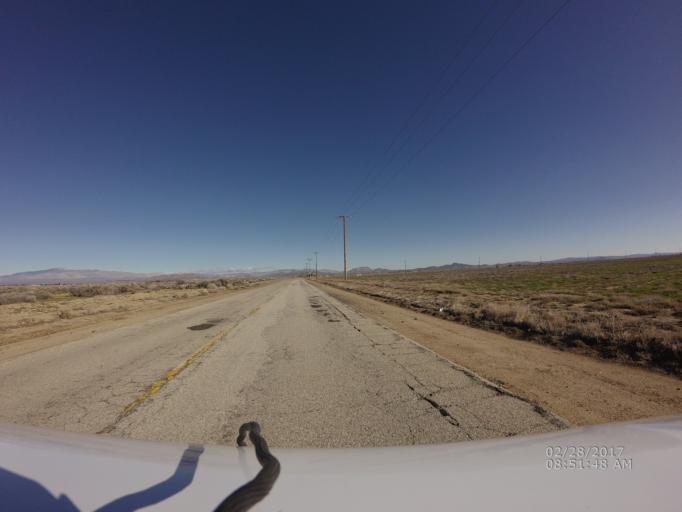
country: US
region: California
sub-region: Kern County
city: Rosamond
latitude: 34.8036
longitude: -118.2376
